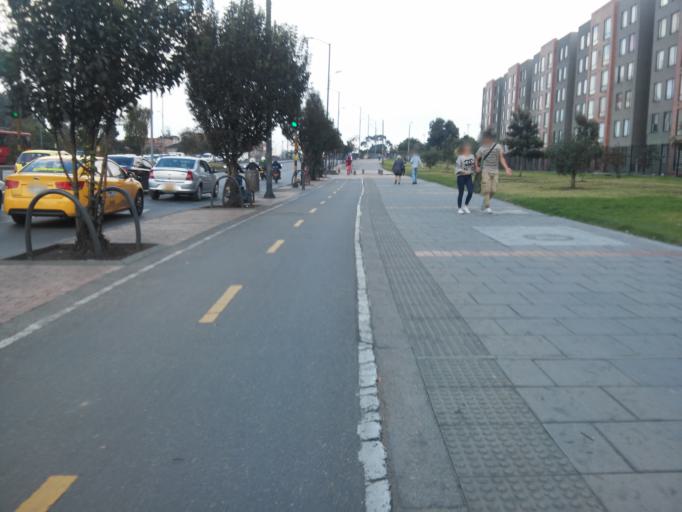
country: CO
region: Cundinamarca
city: Soacha
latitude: 4.5961
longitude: -74.1540
